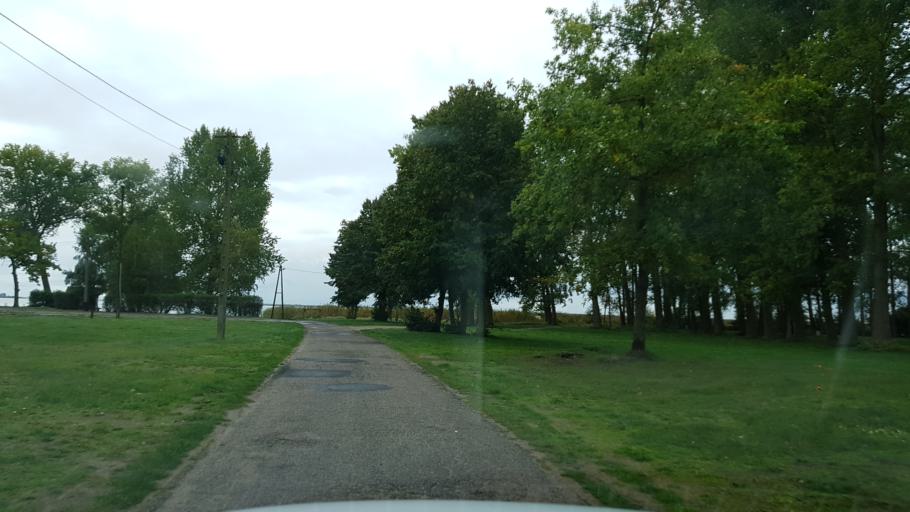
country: PL
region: West Pomeranian Voivodeship
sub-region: Powiat kamienski
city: Wolin
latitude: 53.8299
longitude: 14.5988
